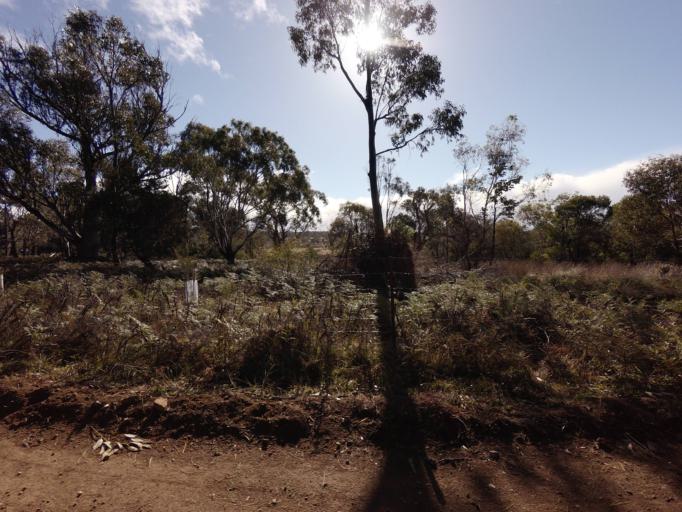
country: AU
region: Tasmania
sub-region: Sorell
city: Sorell
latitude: -42.4015
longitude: 147.9772
